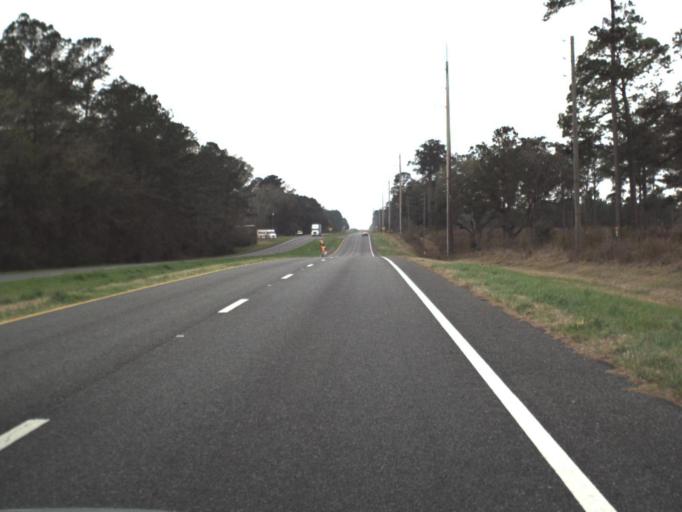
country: US
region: Florida
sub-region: Jefferson County
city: Monticello
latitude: 30.4059
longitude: -84.0076
